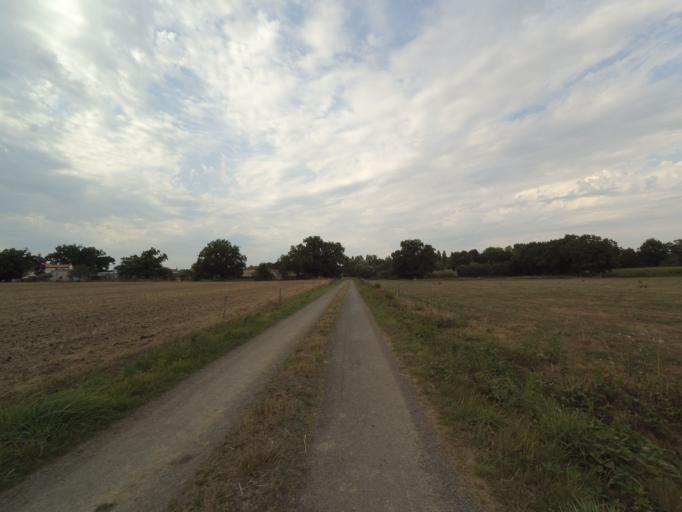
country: FR
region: Pays de la Loire
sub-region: Departement de la Vendee
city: Bouffere
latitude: 46.9811
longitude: -1.3664
